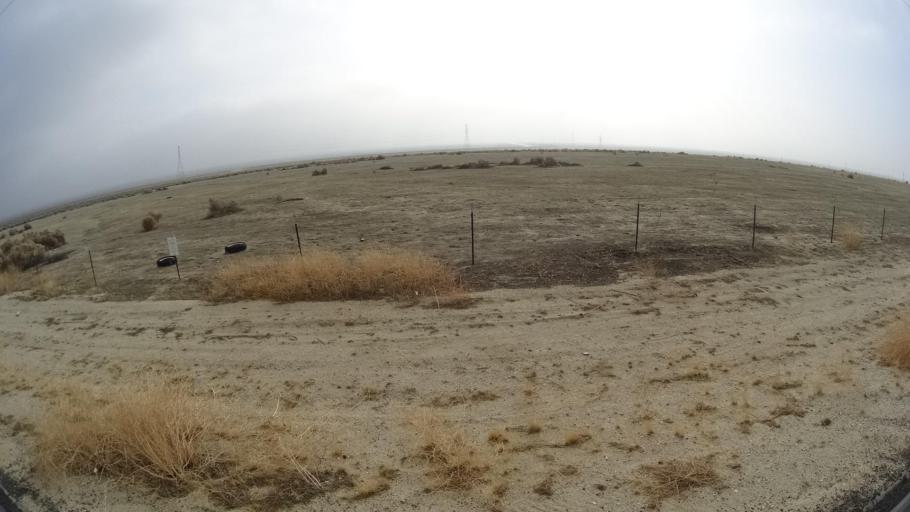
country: US
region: California
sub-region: Kern County
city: Ford City
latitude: 35.2329
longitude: -119.3546
